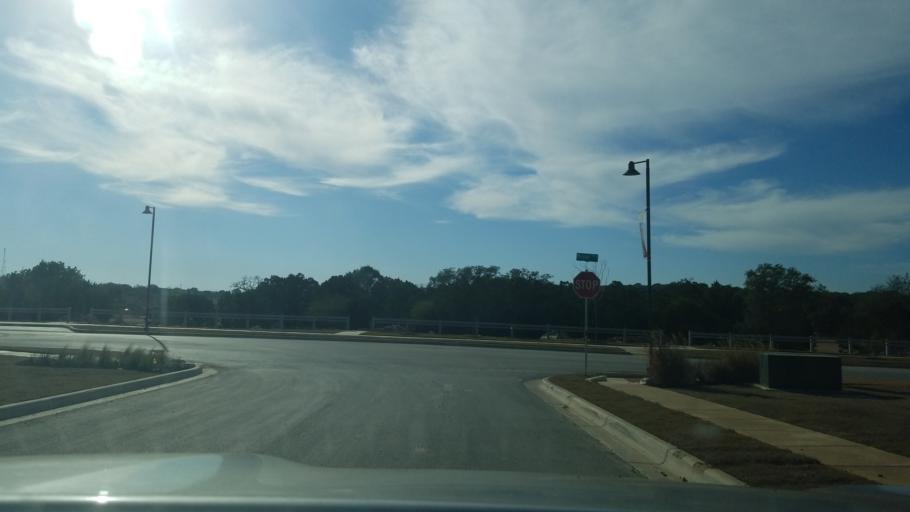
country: US
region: Texas
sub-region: Comal County
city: Canyon Lake
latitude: 29.7803
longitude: -98.2873
